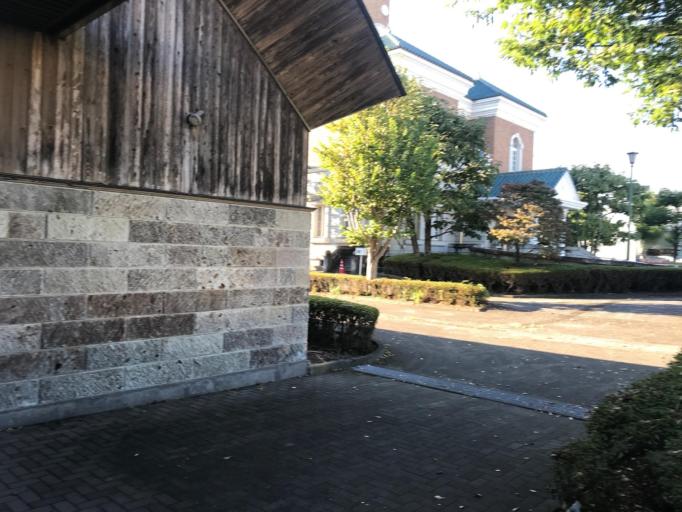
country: JP
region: Tochigi
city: Kanuma
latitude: 36.5695
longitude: 139.7538
